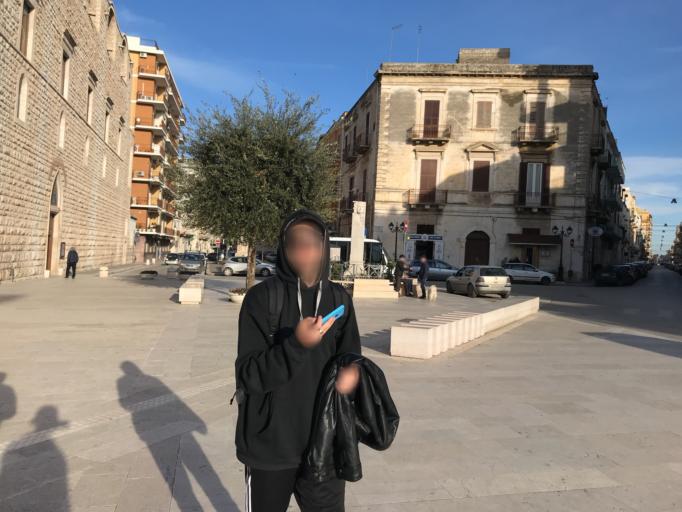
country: IT
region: Apulia
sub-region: Provincia di Bari
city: Corato
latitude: 41.1535
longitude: 16.4134
